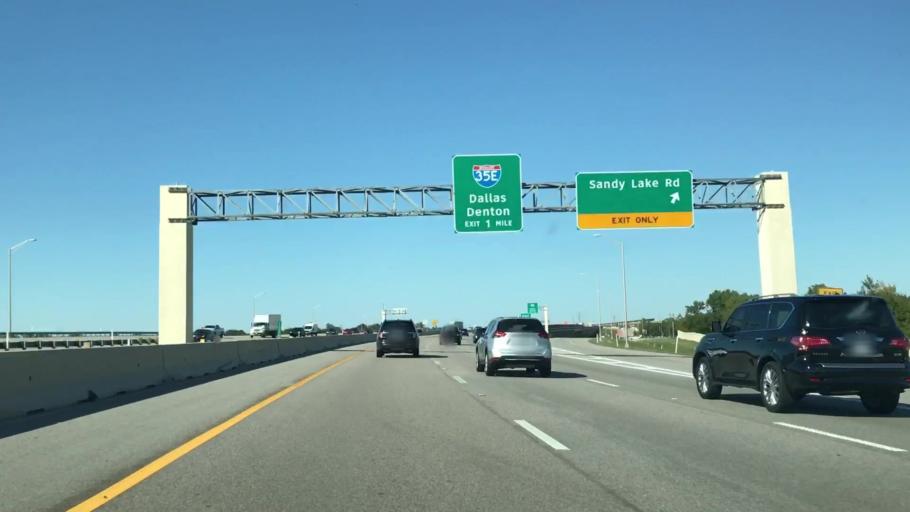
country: US
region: Texas
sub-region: Dallas County
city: Carrollton
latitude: 32.9639
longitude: -96.9324
